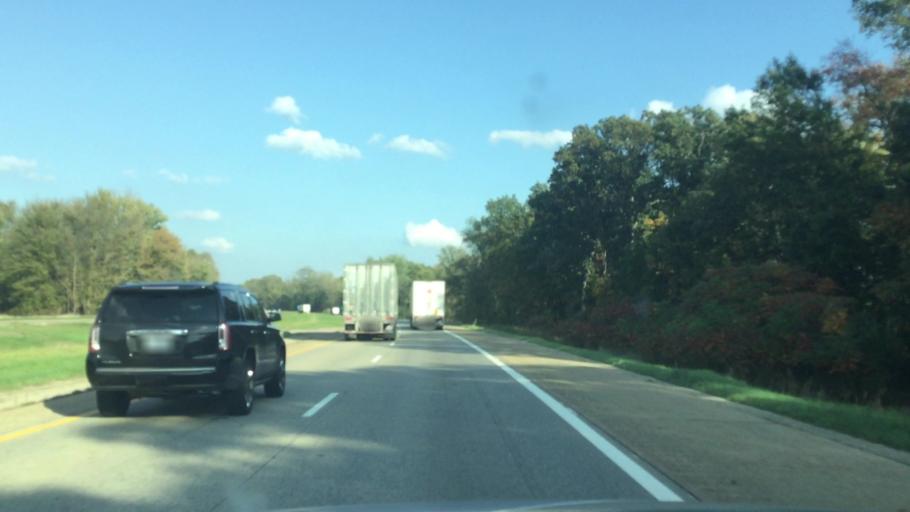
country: US
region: Michigan
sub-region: Jackson County
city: Concord
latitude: 42.2622
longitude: -84.6339
